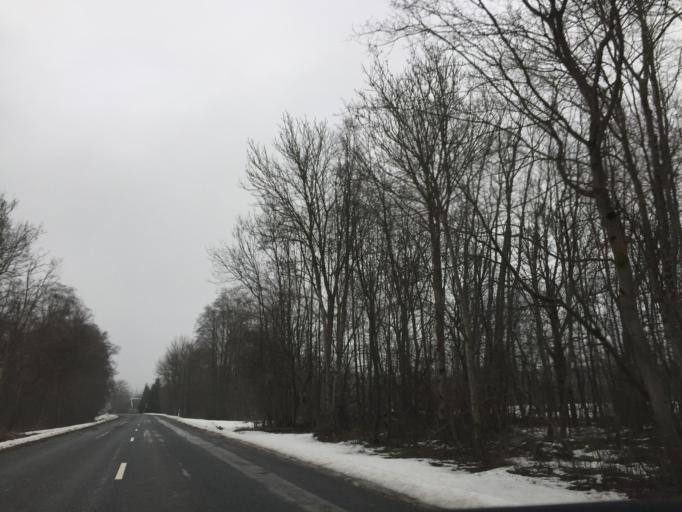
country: EE
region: Saare
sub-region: Kuressaare linn
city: Kuressaare
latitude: 58.3538
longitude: 22.8049
